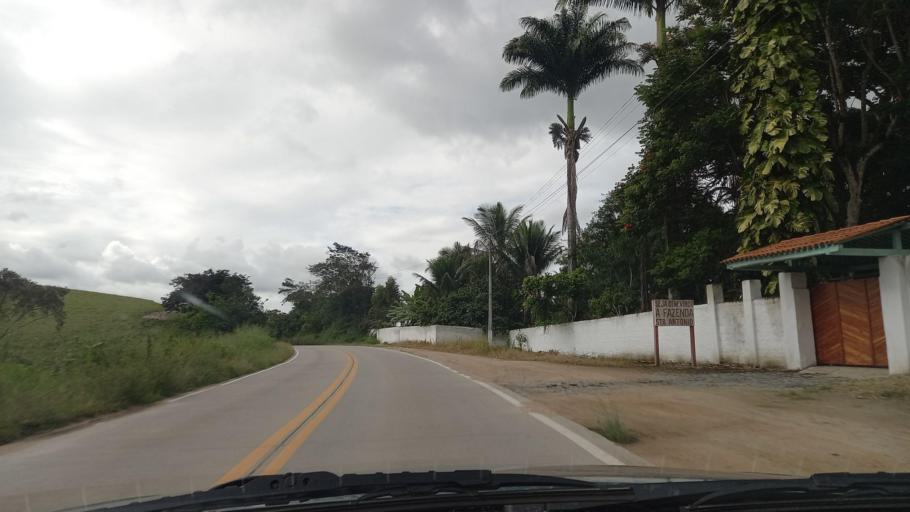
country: BR
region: Pernambuco
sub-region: Quipapa
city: Quipapa
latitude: -8.7926
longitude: -35.9932
